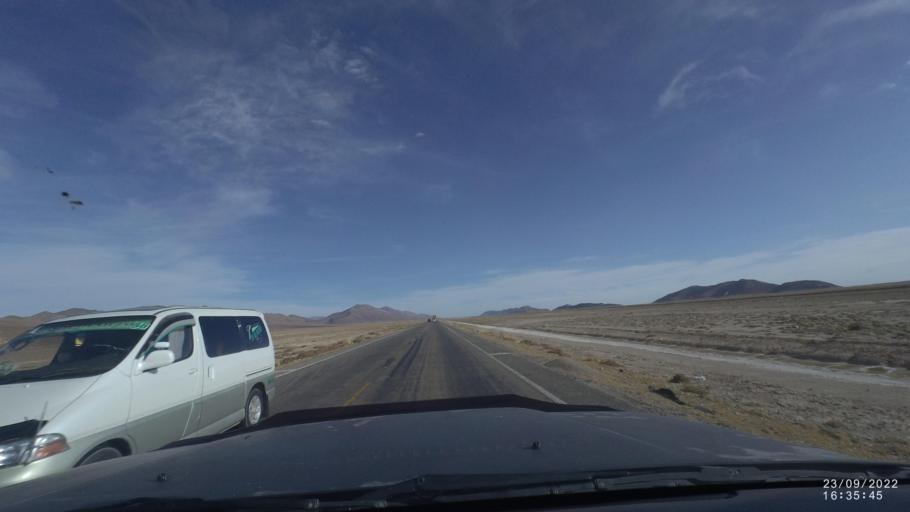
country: BO
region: Oruro
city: Machacamarca
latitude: -18.2092
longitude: -67.0101
